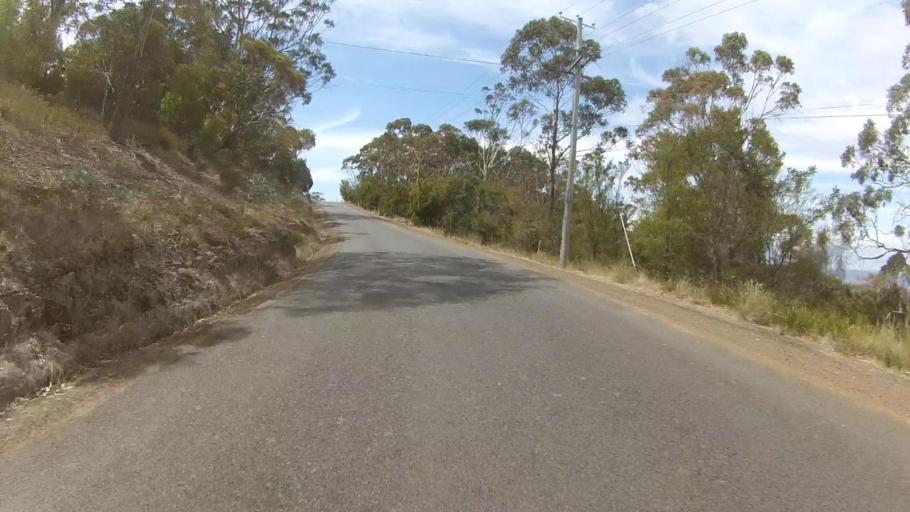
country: AU
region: Tasmania
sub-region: Kingborough
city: Blackmans Bay
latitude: -43.0522
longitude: 147.3393
